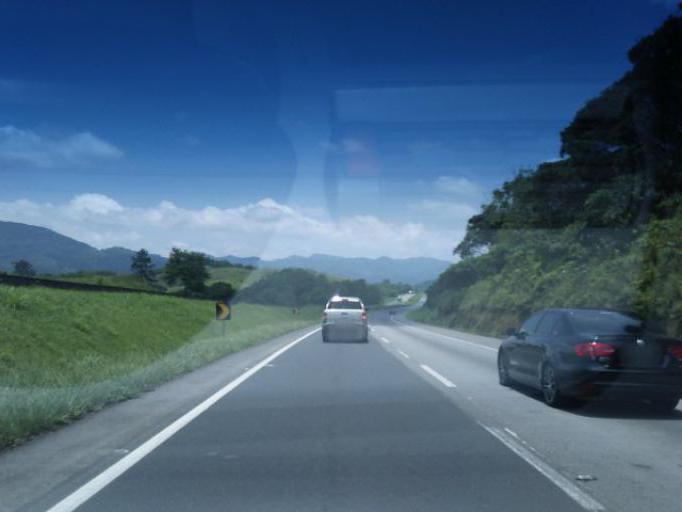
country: BR
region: Sao Paulo
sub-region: Miracatu
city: Miracatu
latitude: -24.2413
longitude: -47.3632
